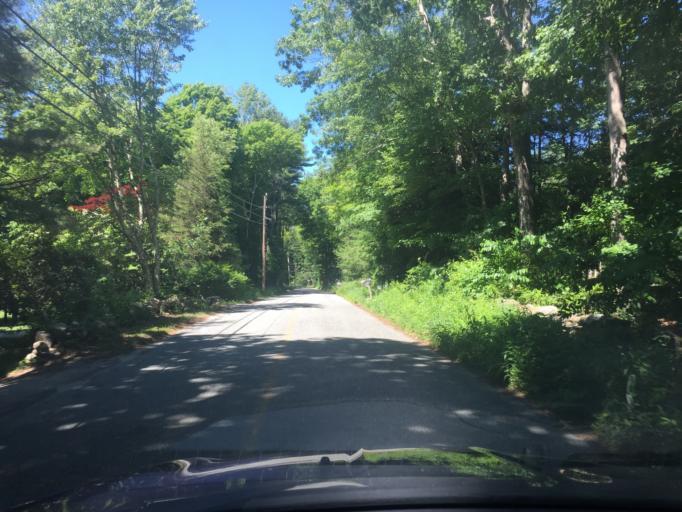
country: US
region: Rhode Island
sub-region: Washington County
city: Hopkinton
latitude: 41.4801
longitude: -71.8095
